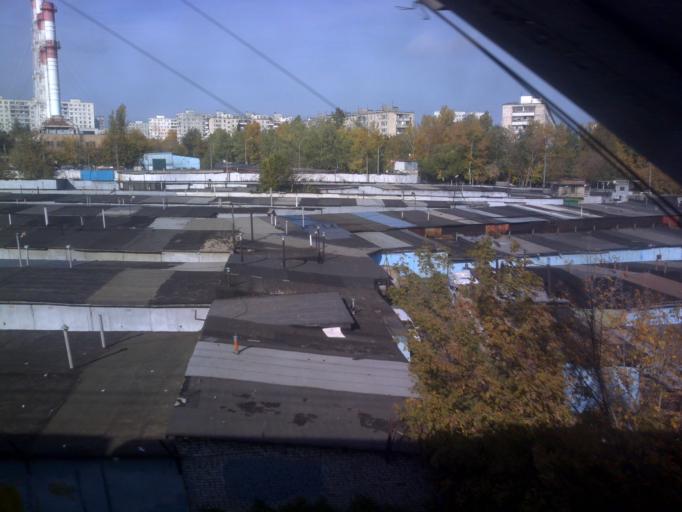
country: RU
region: Moskovskaya
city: Biryulevo Zapadnoye
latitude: 55.5989
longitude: 37.6276
